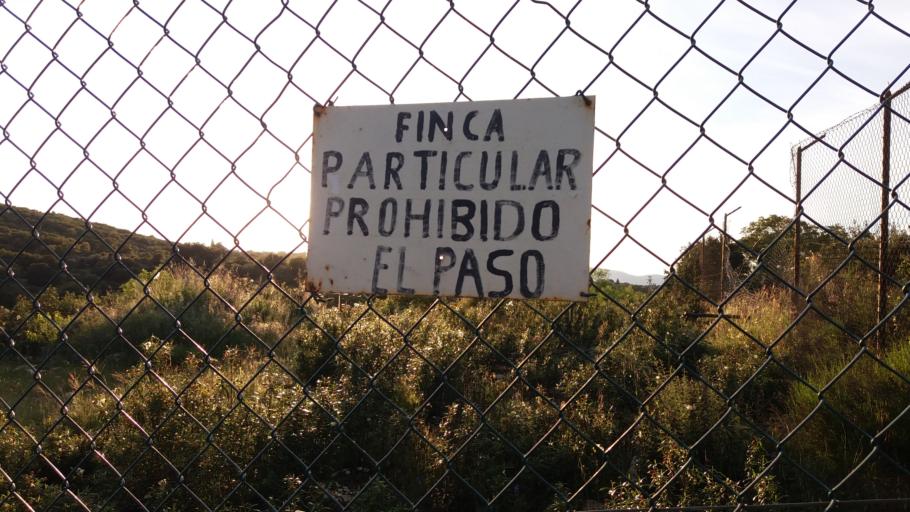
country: ES
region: Madrid
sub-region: Provincia de Madrid
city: Galapagar
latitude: 40.5894
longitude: -3.9702
